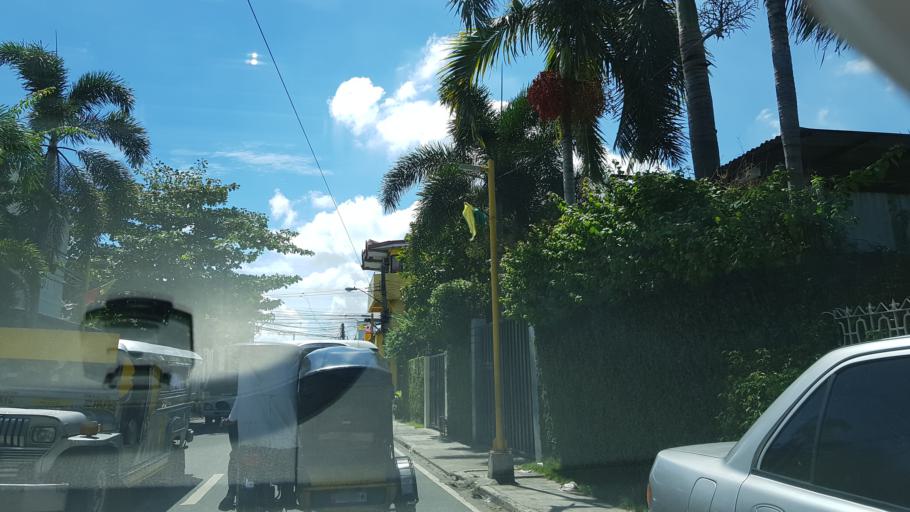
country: PH
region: Calabarzon
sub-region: Province of Rizal
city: Pateros
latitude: 14.5354
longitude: 121.0688
